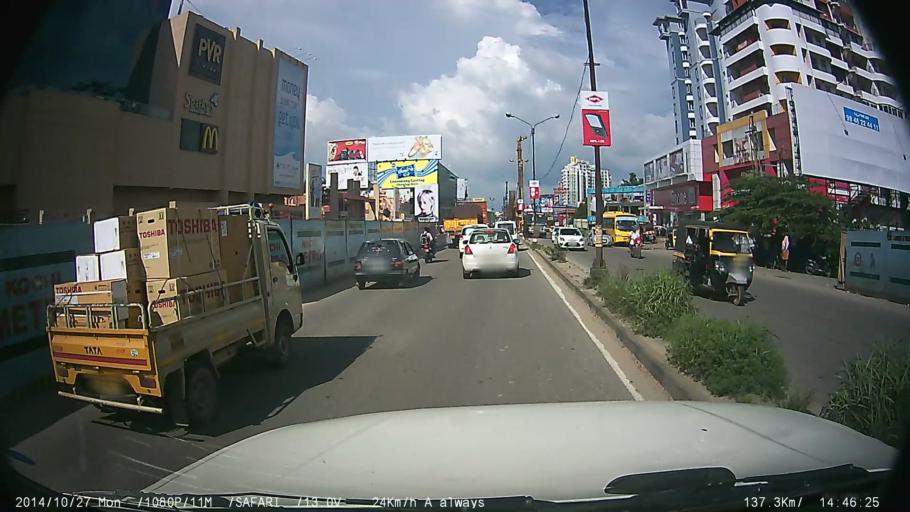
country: IN
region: Kerala
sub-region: Ernakulam
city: Elur
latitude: 10.0257
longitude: 76.3087
